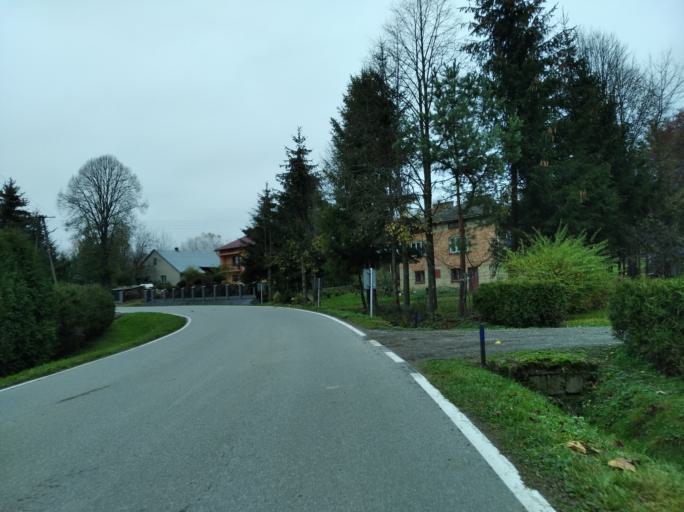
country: PL
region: Subcarpathian Voivodeship
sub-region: Powiat krosnienski
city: Leki
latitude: 49.8101
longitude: 21.6580
